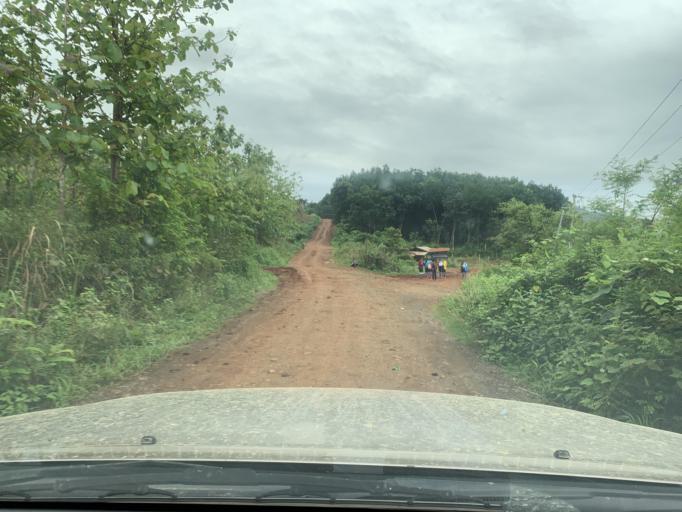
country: TH
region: Nan
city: Mae Charim
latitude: 18.4120
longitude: 101.4411
